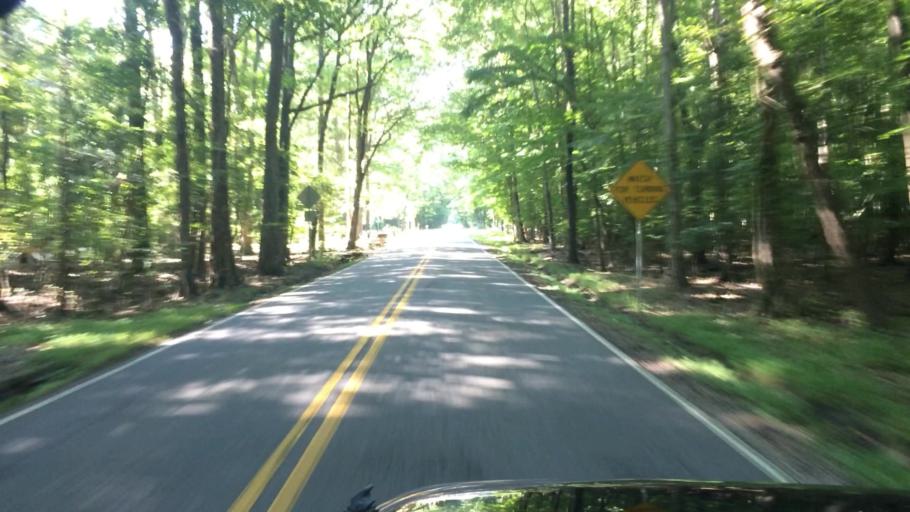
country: US
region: Virginia
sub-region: James City County
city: Williamsburg
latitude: 37.2448
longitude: -76.7955
